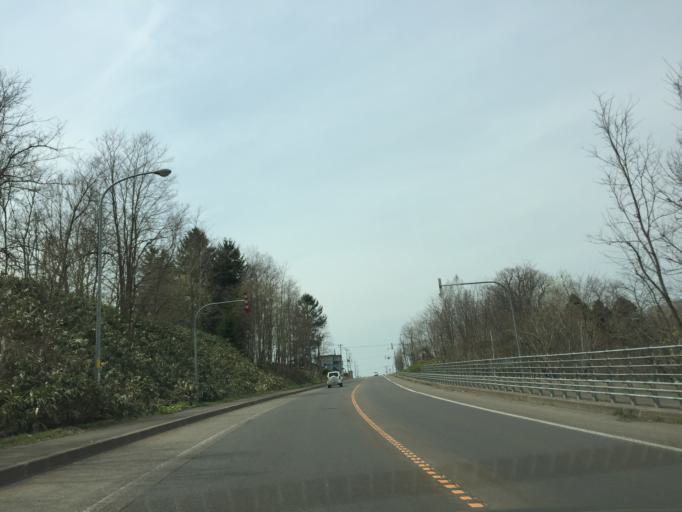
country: JP
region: Hokkaido
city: Akabira
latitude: 43.5360
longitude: 142.0966
